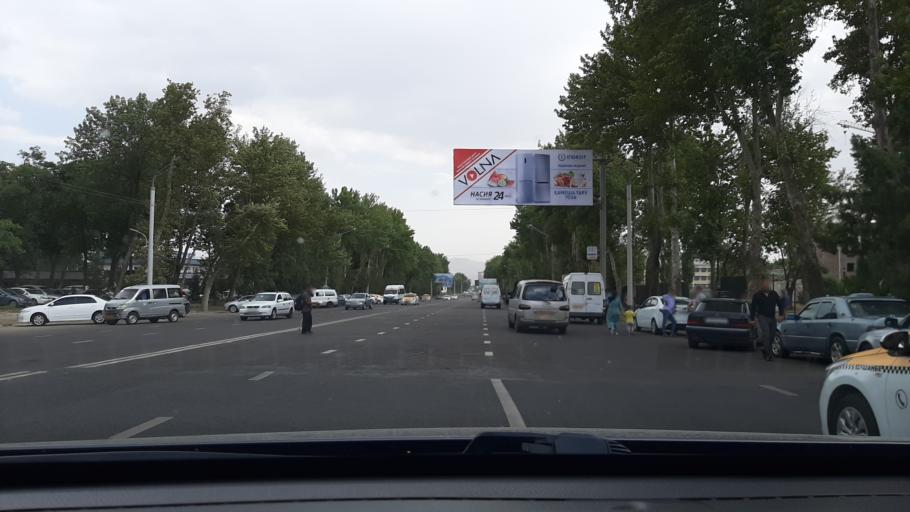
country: TJ
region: Dushanbe
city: Dushanbe
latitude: 38.5817
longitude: 68.7550
